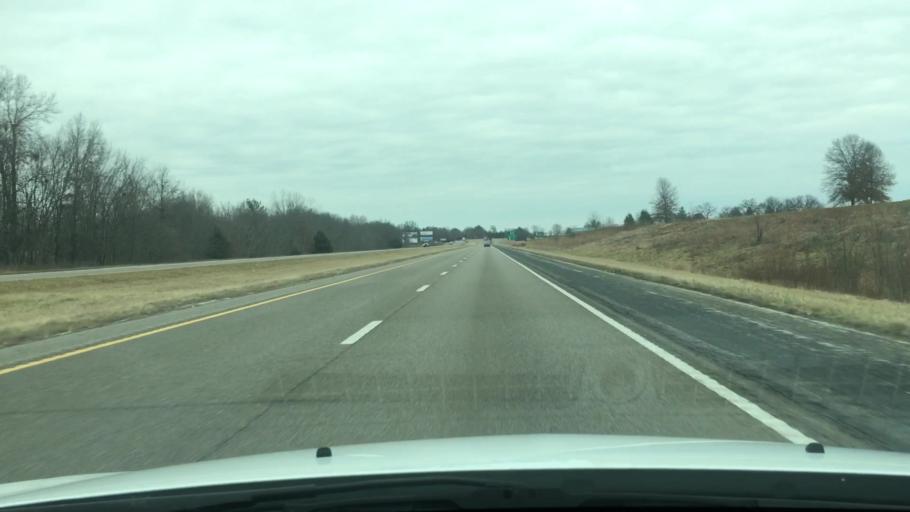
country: US
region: Missouri
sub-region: Callaway County
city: Fulton
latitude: 38.9979
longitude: -91.8935
